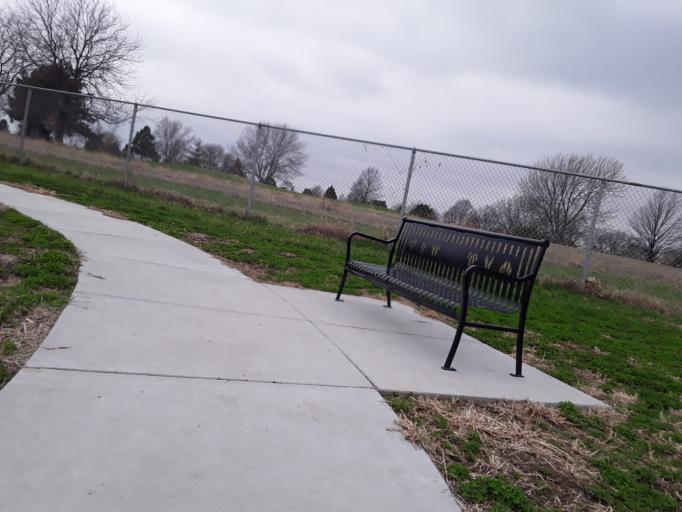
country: US
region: Nebraska
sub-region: Lancaster County
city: Lincoln
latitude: 40.8474
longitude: -96.6073
